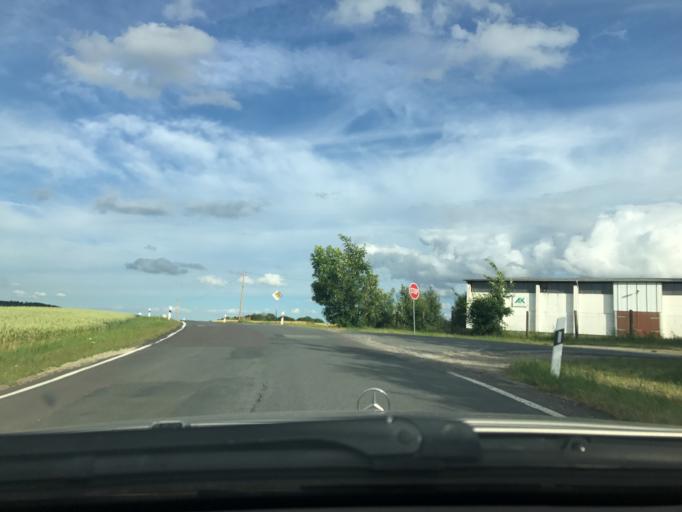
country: DE
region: Thuringia
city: Geisleden
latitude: 51.3172
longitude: 10.1787
